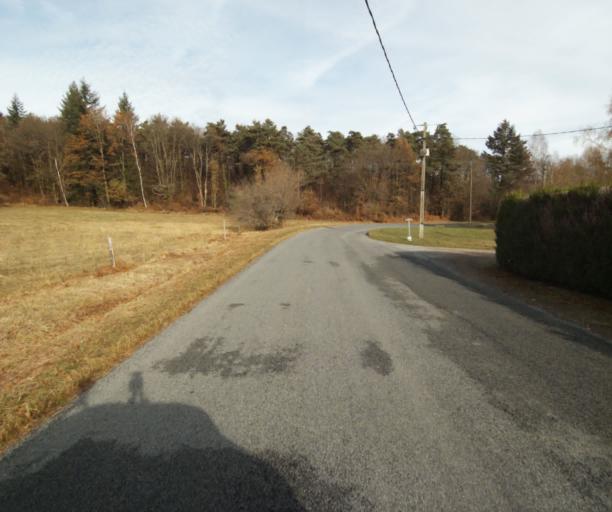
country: FR
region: Limousin
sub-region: Departement de la Correze
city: Sainte-Fortunade
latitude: 45.1780
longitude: 1.7452
